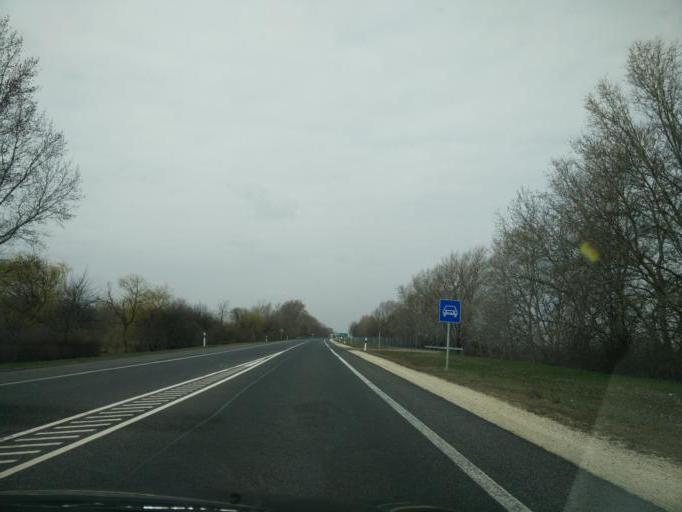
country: HU
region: Gyor-Moson-Sopron
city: Per
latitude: 47.6903
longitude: 17.7971
